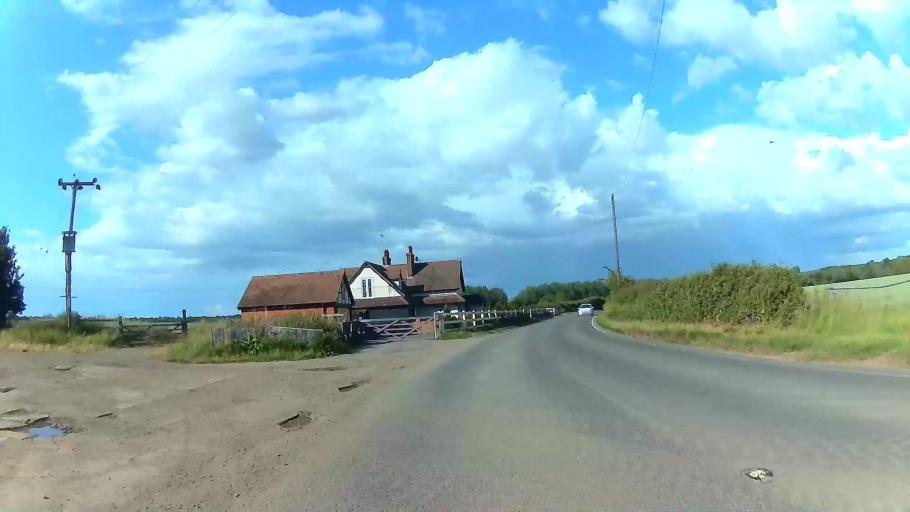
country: GB
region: England
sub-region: Essex
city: Kelvedon Hatch
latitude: 51.6882
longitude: 0.3093
